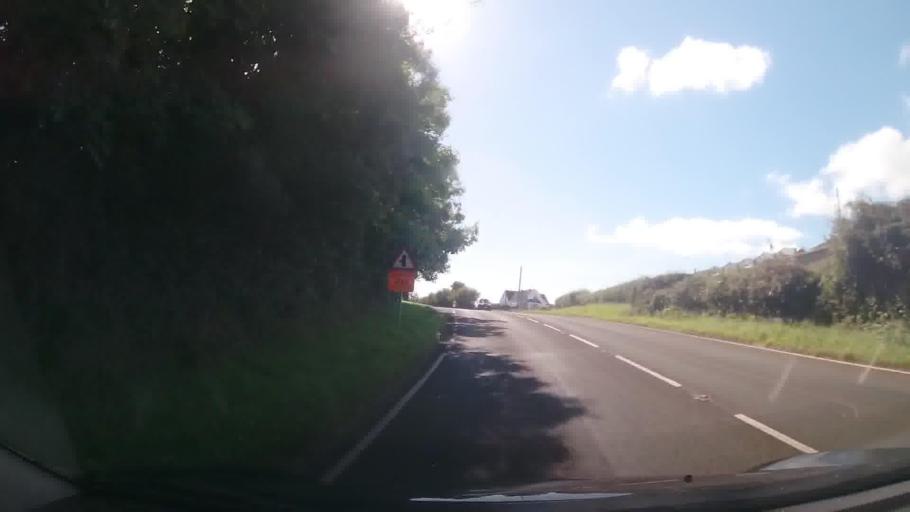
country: GB
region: Wales
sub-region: Pembrokeshire
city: Penally
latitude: 51.6675
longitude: -4.7236
